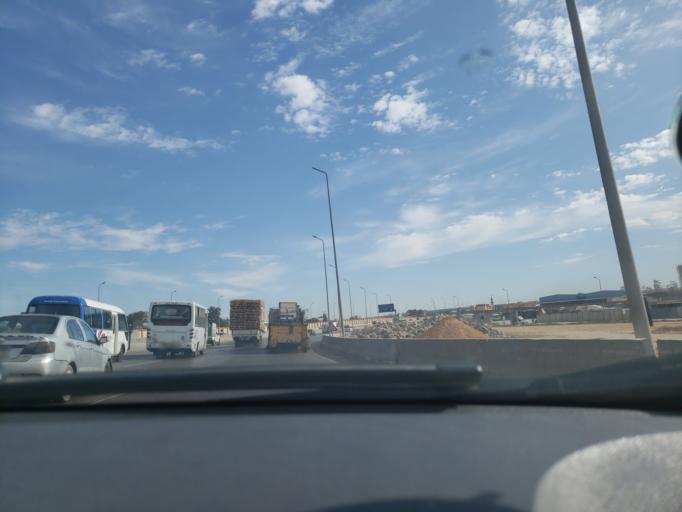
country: EG
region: Muhafazat al Qalyubiyah
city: Al Khankah
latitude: 30.1479
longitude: 31.4333
